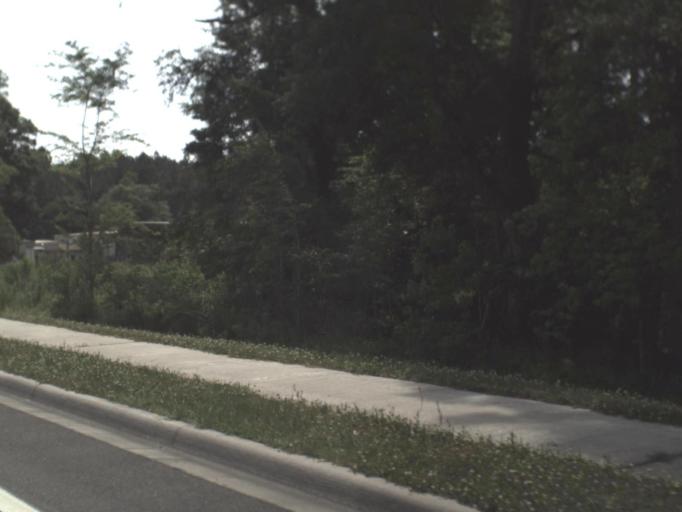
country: US
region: Florida
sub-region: Nassau County
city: Callahan
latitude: 30.5847
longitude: -81.8024
